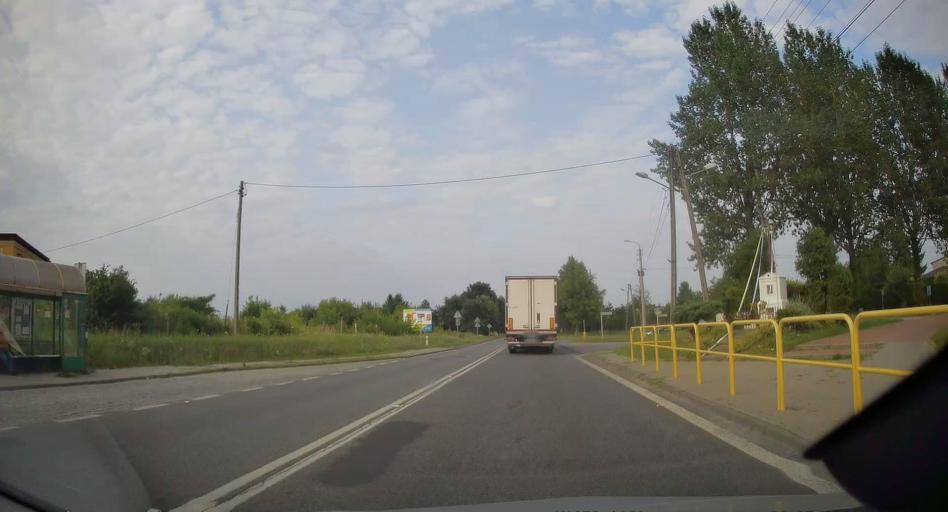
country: PL
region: Silesian Voivodeship
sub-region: Powiat czestochowski
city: Redziny
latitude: 50.8659
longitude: 19.2274
